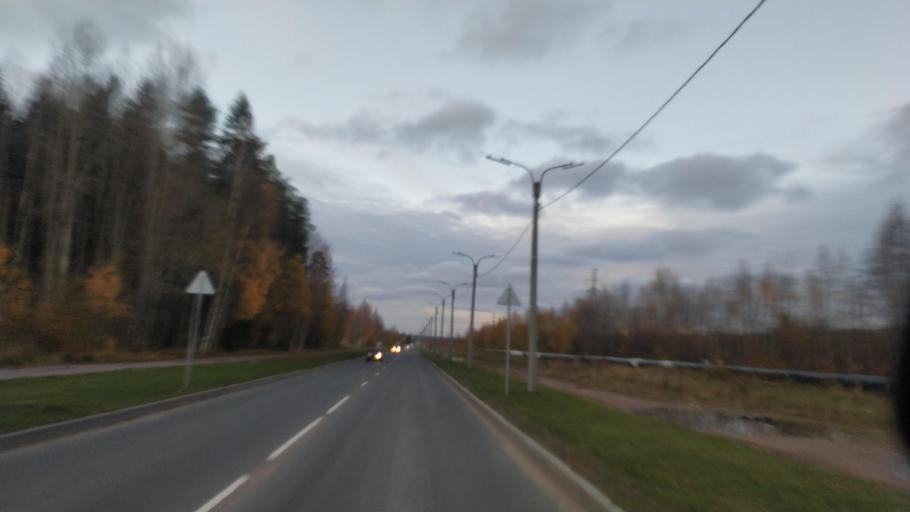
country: RU
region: Leningrad
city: Sosnovyy Bor
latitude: 59.9086
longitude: 29.1016
